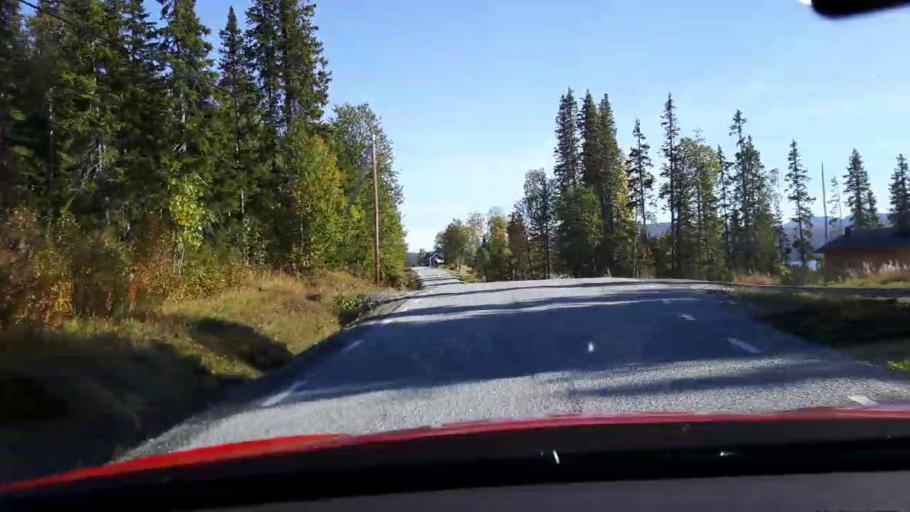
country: NO
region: Nord-Trondelag
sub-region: Royrvik
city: Royrvik
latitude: 64.8132
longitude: 14.1567
